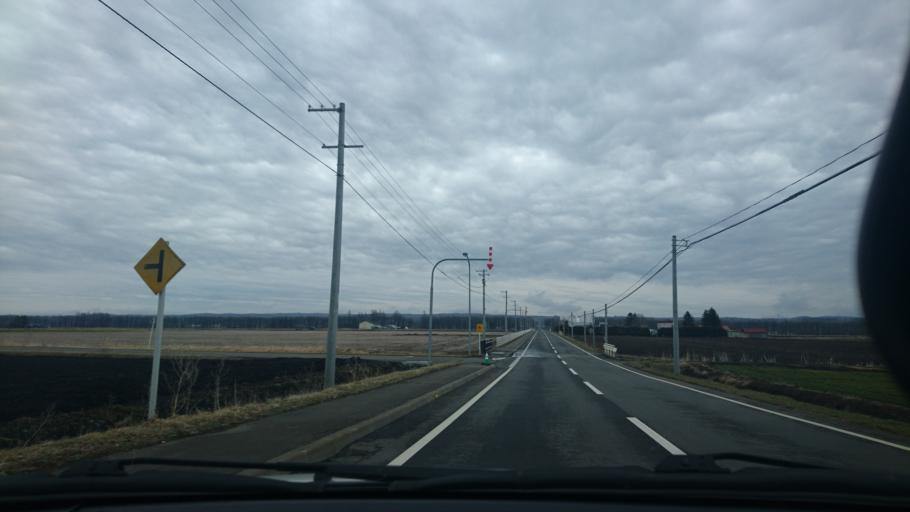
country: JP
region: Hokkaido
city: Otofuke
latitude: 42.9942
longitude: 143.2293
